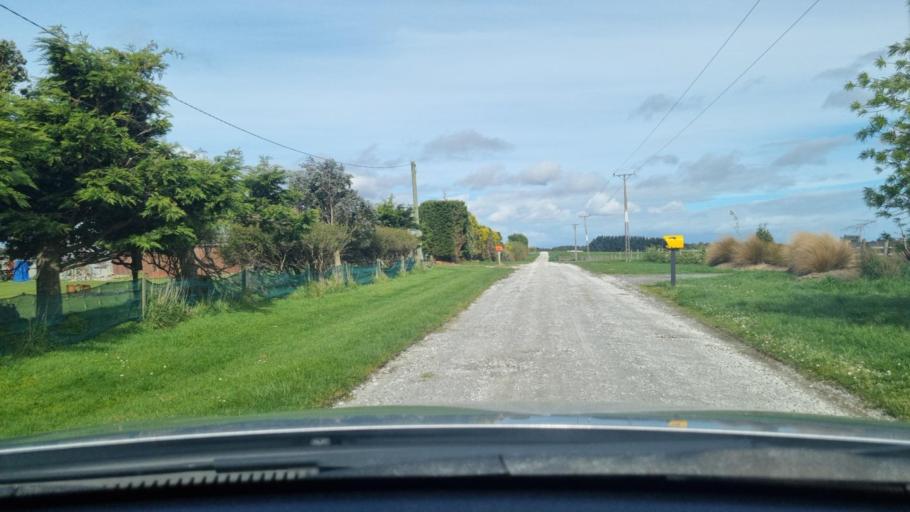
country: NZ
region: Southland
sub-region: Invercargill City
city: Invercargill
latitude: -46.4532
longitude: 168.3829
